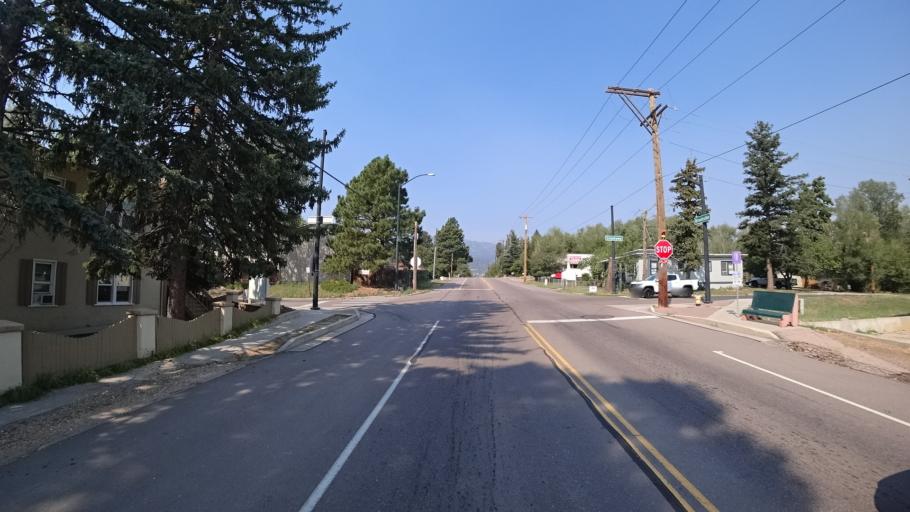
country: US
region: Colorado
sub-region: El Paso County
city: Colorado Springs
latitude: 38.8126
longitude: -104.8328
